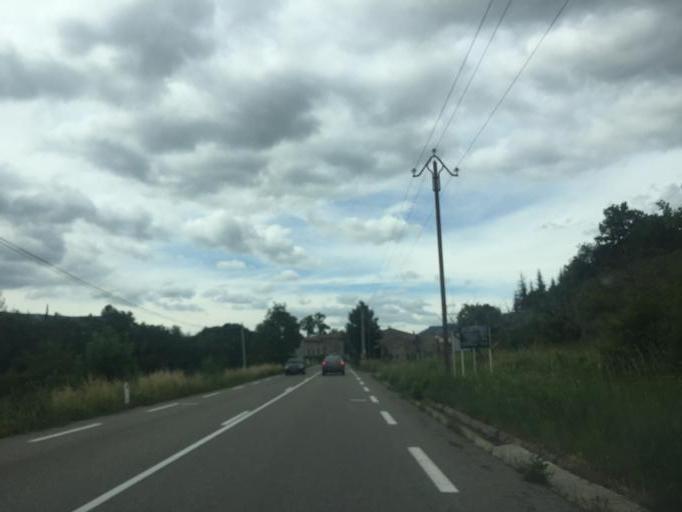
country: FR
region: Rhone-Alpes
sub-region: Departement de l'Ardeche
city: Alba-la-Romaine
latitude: 44.5497
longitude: 4.6079
